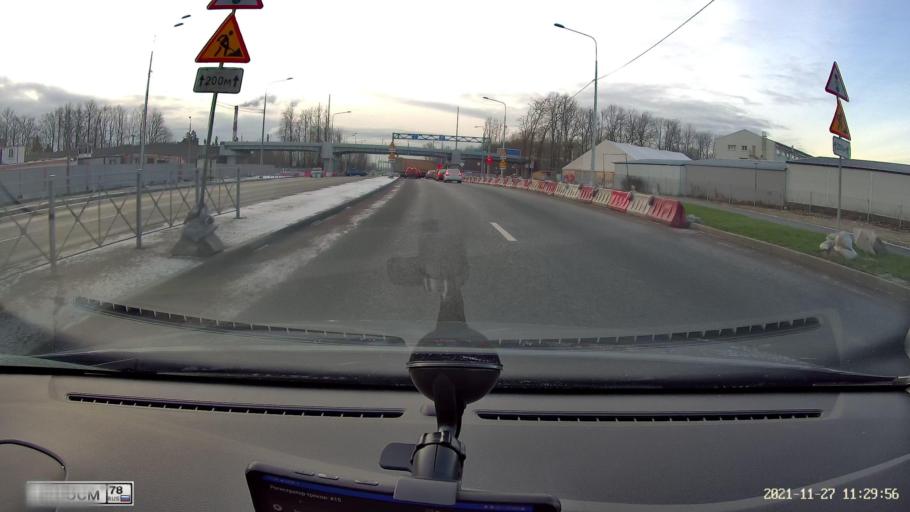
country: RU
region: St.-Petersburg
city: Krasnoye Selo
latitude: 59.7313
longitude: 30.0578
